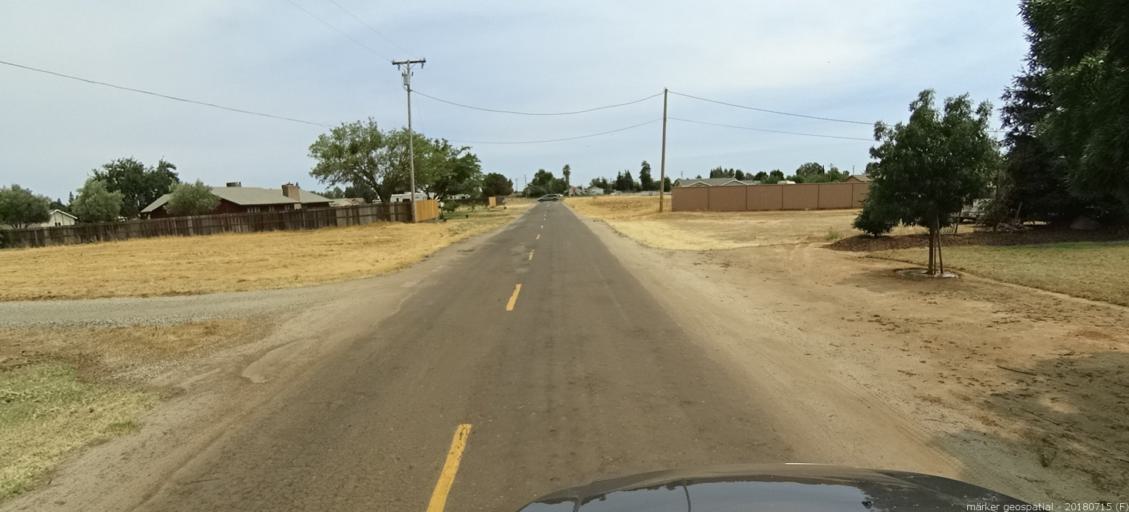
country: US
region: California
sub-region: Madera County
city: Madera Acres
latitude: 37.0061
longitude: -120.1018
